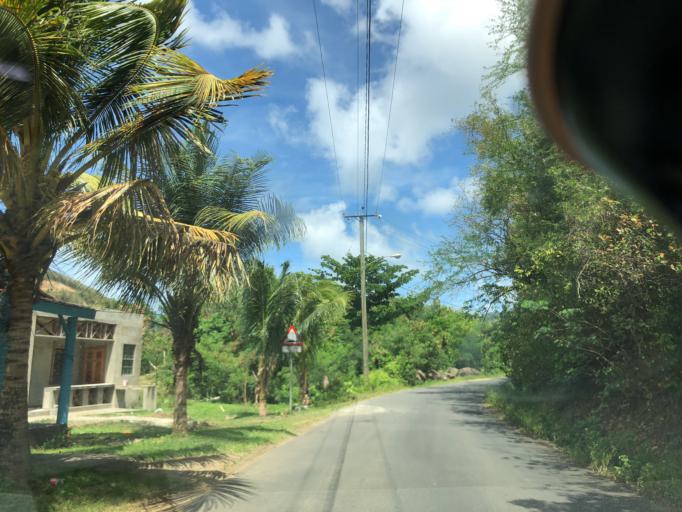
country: LC
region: Gros-Islet
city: Gros Islet
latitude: 14.0630
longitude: -60.9689
